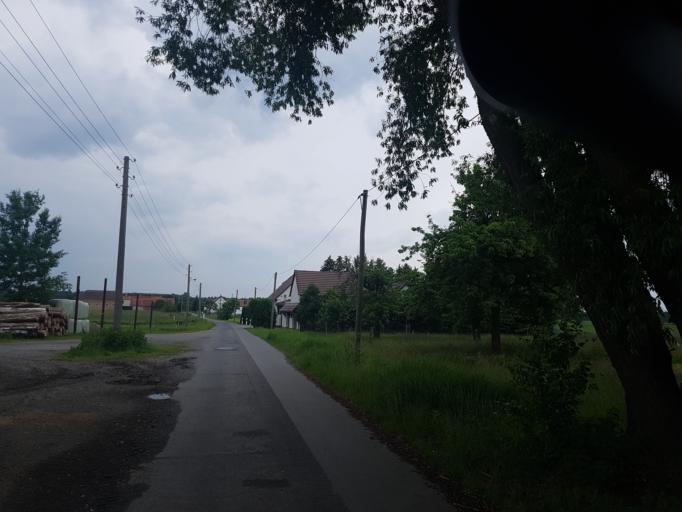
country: DE
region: Brandenburg
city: Finsterwalde
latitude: 51.5671
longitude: 13.6645
